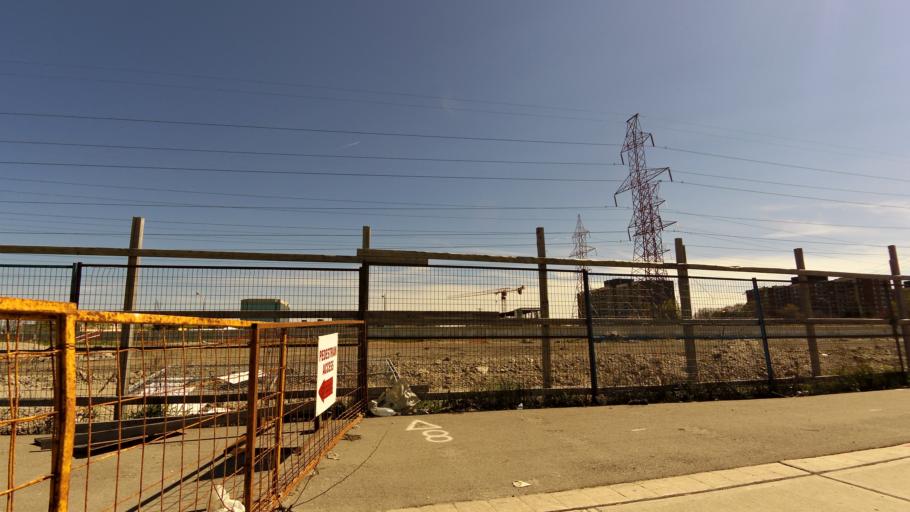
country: CA
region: Ontario
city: Concord
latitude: 43.7674
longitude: -79.4909
